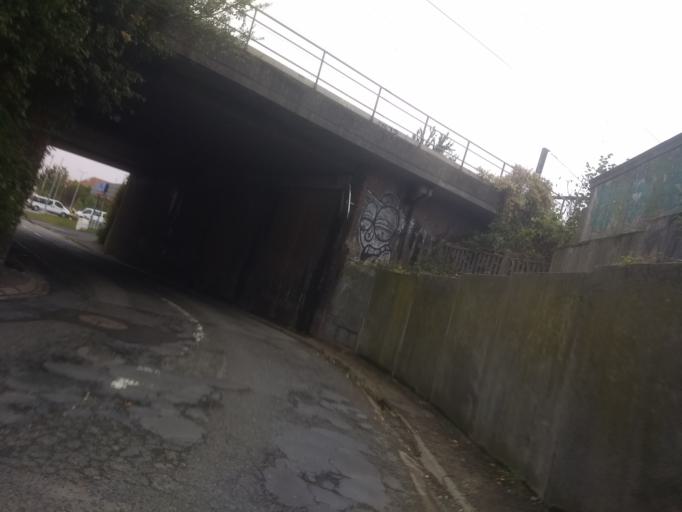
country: FR
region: Nord-Pas-de-Calais
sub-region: Departement du Pas-de-Calais
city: Arras
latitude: 50.2915
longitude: 2.7943
